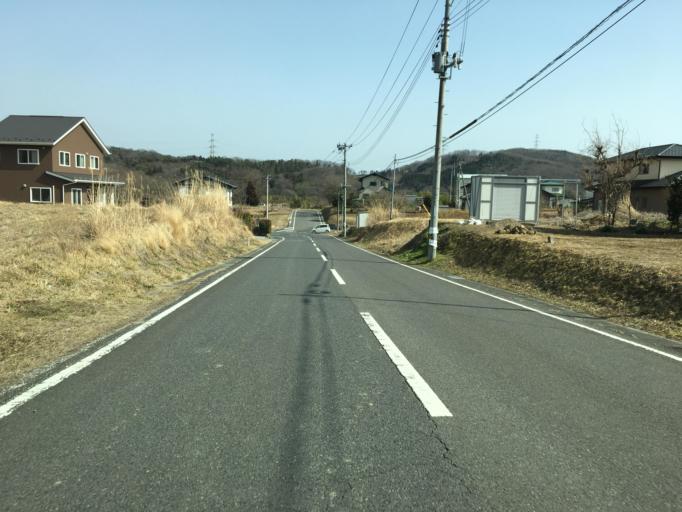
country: JP
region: Fukushima
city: Motomiya
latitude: 37.5257
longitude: 140.4089
